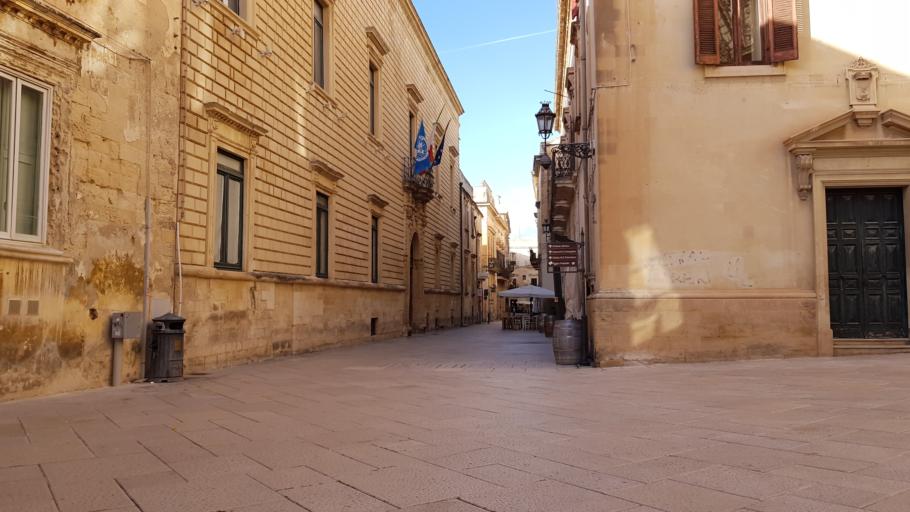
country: IT
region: Apulia
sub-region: Provincia di Lecce
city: Lecce
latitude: 40.3549
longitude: 18.1728
